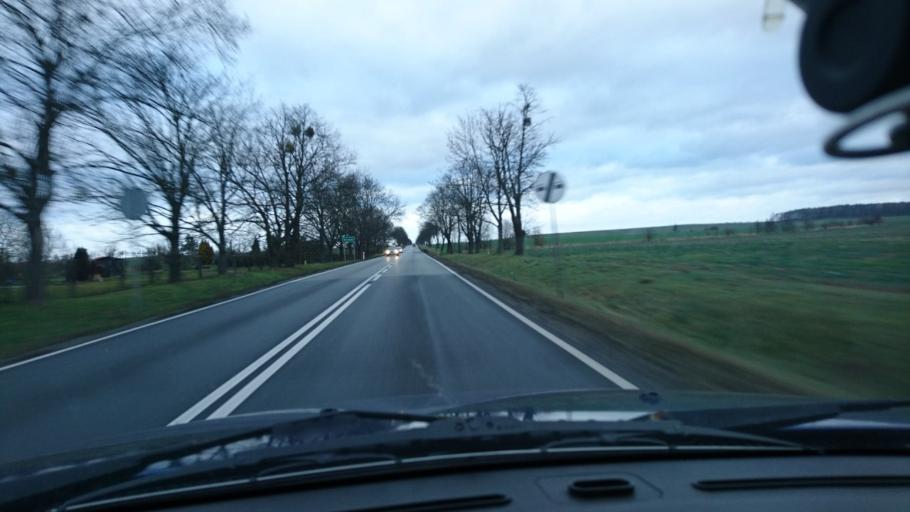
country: PL
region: Opole Voivodeship
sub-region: Powiat kluczborski
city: Byczyna
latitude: 51.0849
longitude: 18.1983
